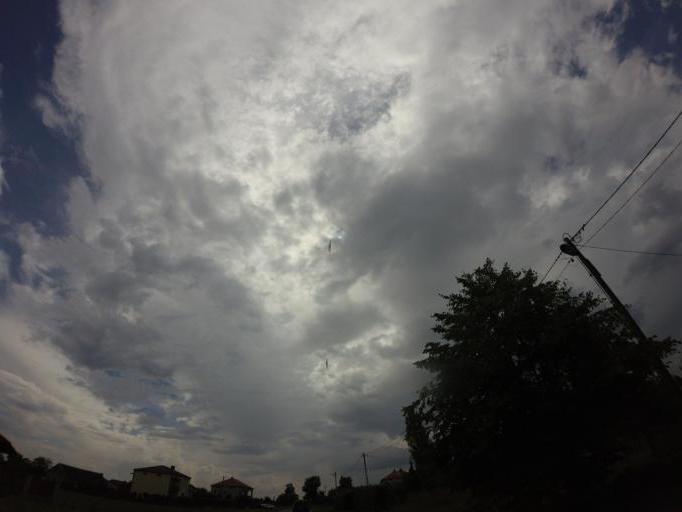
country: PL
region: Swietokrzyskie
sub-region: Powiat staszowski
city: Bogoria
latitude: 50.6254
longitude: 21.2271
